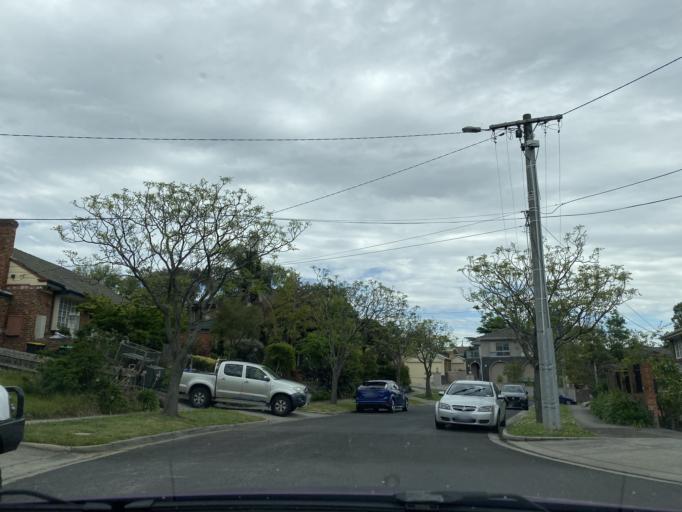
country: AU
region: Victoria
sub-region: Manningham
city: Templestowe Lower
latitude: -37.7607
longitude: 145.1209
